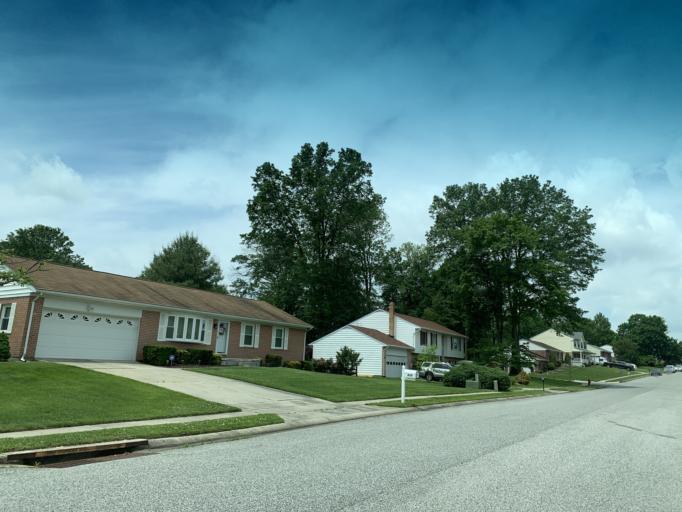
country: US
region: Maryland
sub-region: Harford County
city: South Bel Air
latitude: 39.5418
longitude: -76.2998
